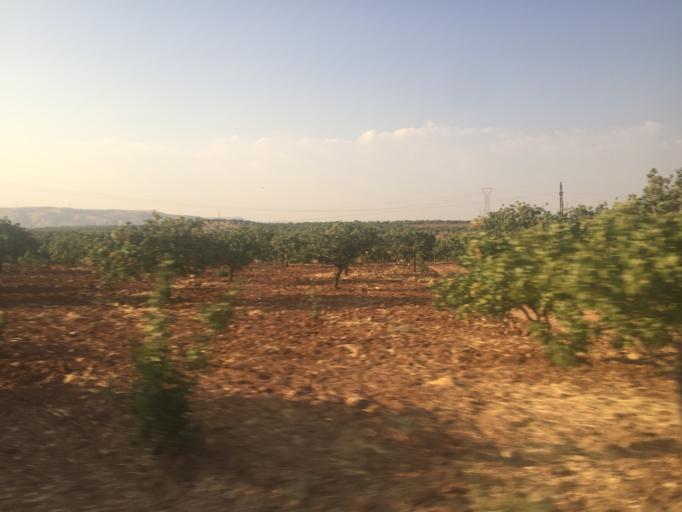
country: TR
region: Gaziantep
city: Nizip
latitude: 37.0142
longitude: 37.8445
